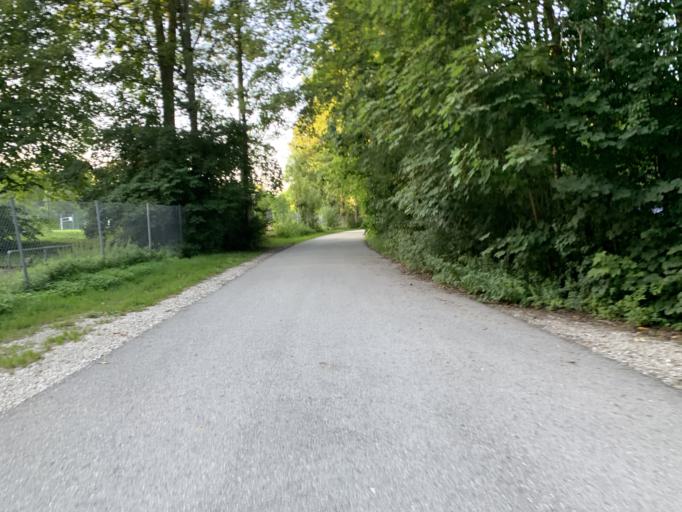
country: DE
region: Bavaria
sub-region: Upper Bavaria
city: Freising
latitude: 48.3874
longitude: 11.7503
